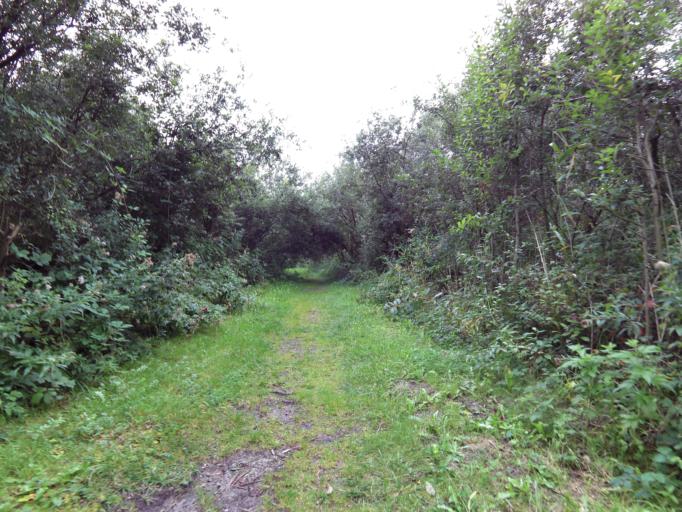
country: NL
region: South Holland
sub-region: Gemeente Goeree-Overflakkee
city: Dirksland
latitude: 51.7662
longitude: 4.0370
